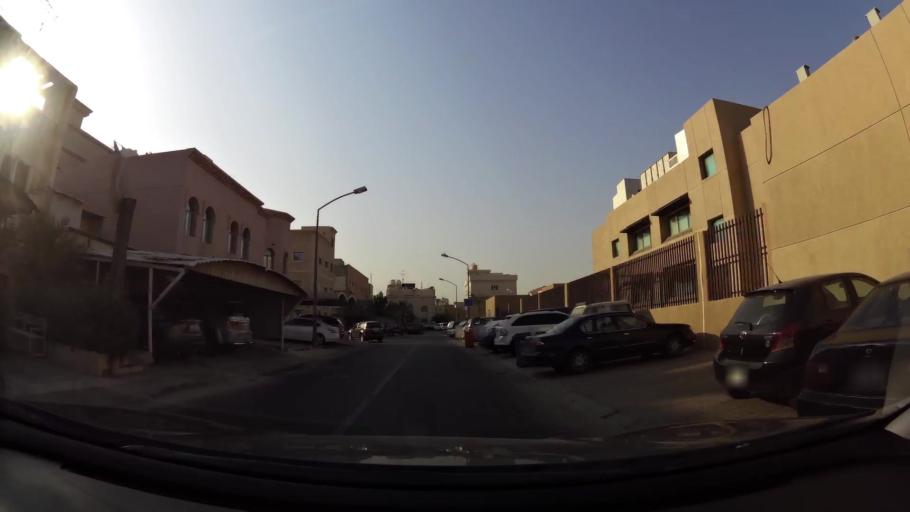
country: KW
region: Al Asimah
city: Ad Dasmah
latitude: 29.3638
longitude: 47.9988
